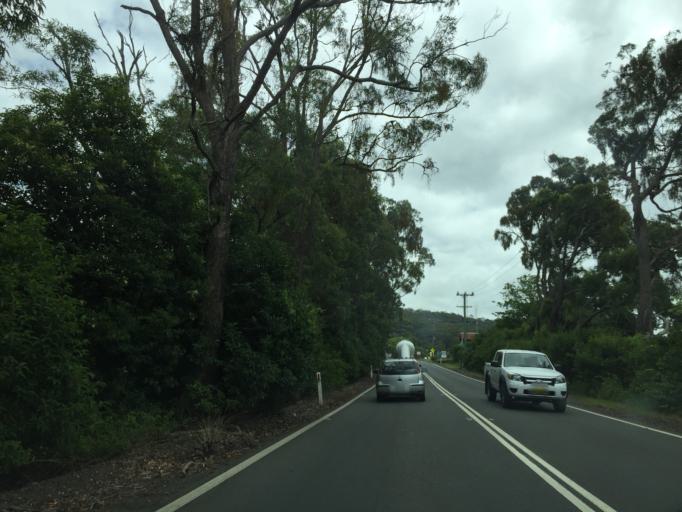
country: AU
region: New South Wales
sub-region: Hawkesbury
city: Richmond
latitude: -33.5437
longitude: 150.6463
